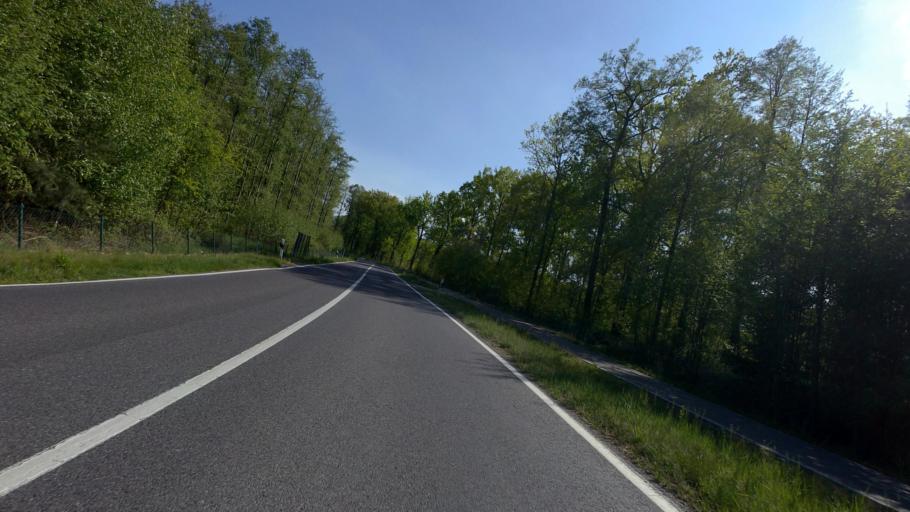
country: DE
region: Saxony
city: Ossling
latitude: 51.3417
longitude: 14.1547
